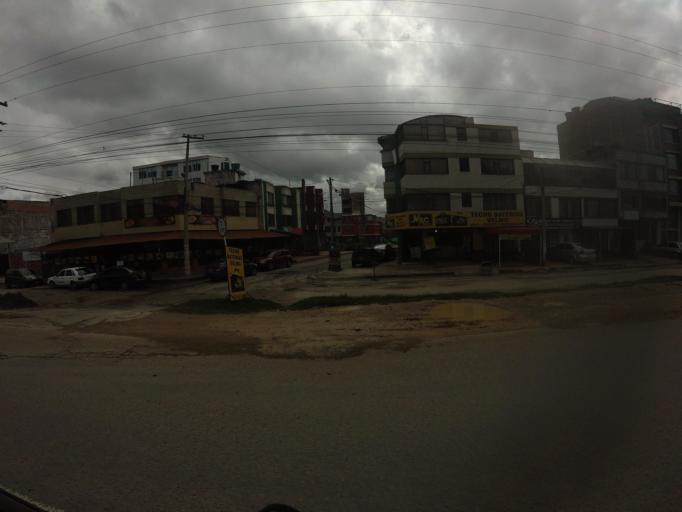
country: CO
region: Boyaca
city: Duitama
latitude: 5.8088
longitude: -73.0284
